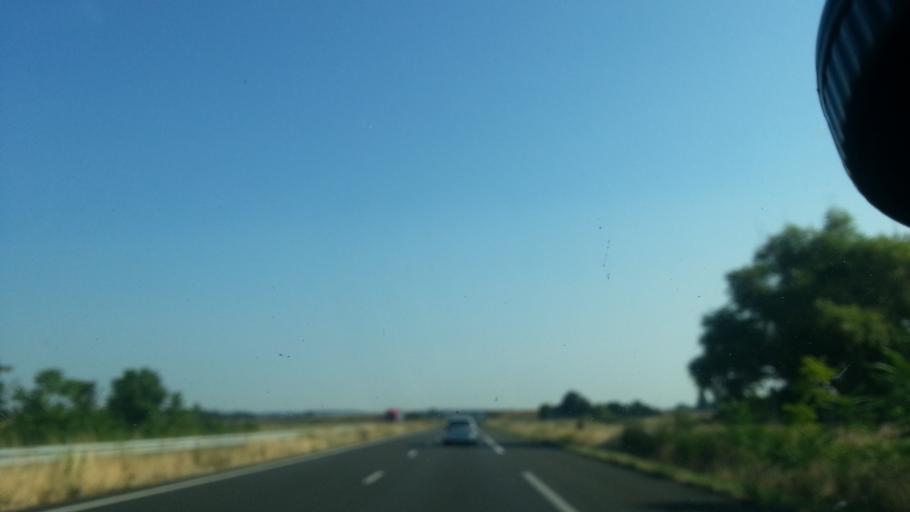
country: FR
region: Poitou-Charentes
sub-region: Departement de la Vienne
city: Chatellerault
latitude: 46.8219
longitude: 0.5177
